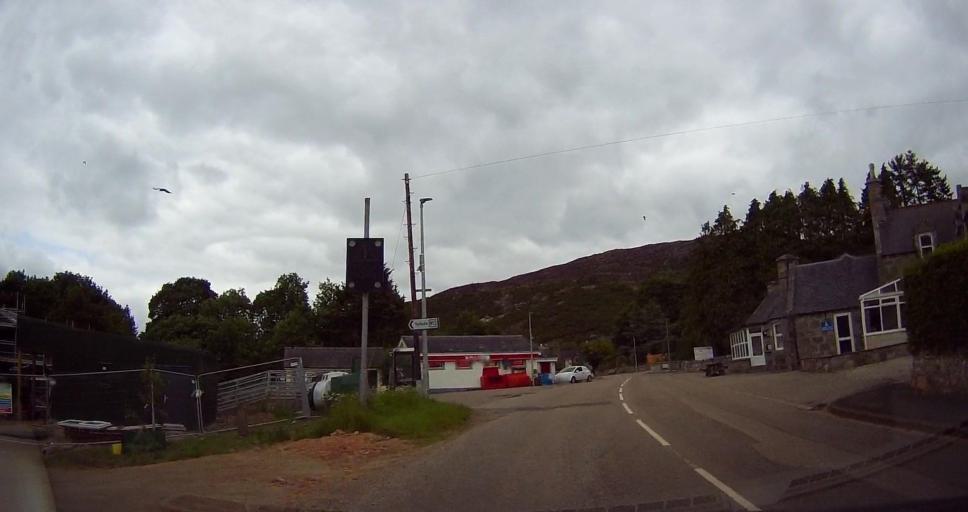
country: GB
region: Scotland
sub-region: Highland
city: Dornoch
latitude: 57.9881
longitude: -4.1554
